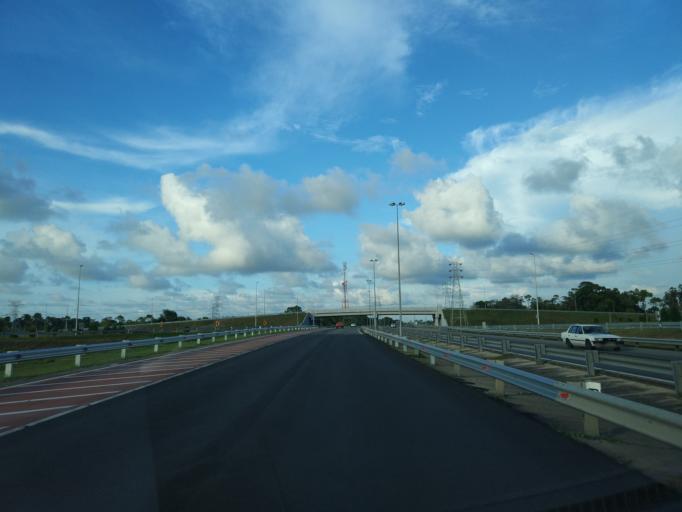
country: BN
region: Tutong
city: Tutong
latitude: 4.7429
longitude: 114.5979
